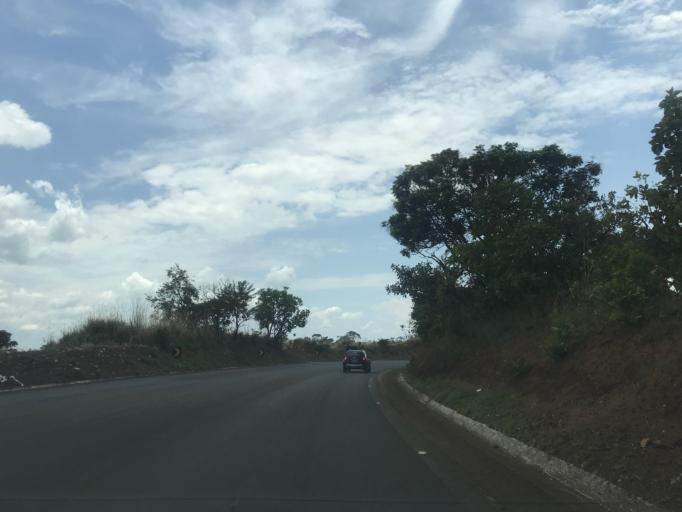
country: BR
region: Goias
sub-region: Vianopolis
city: Vianopolis
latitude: -16.9413
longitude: -48.5570
